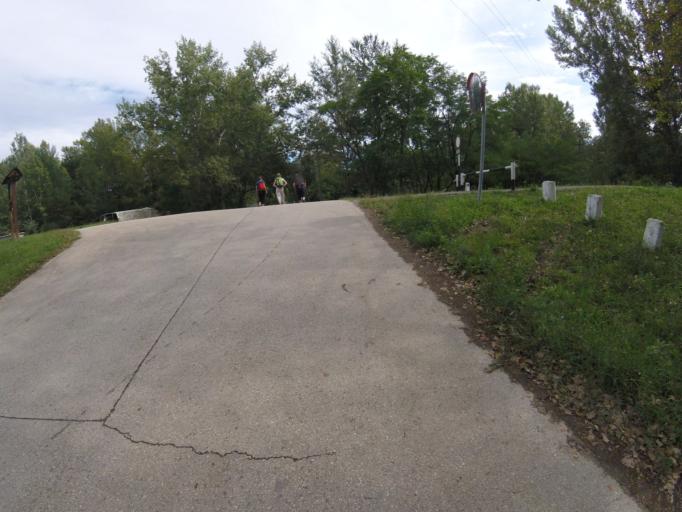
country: HU
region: Pest
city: God
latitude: 47.6619
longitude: 19.1085
